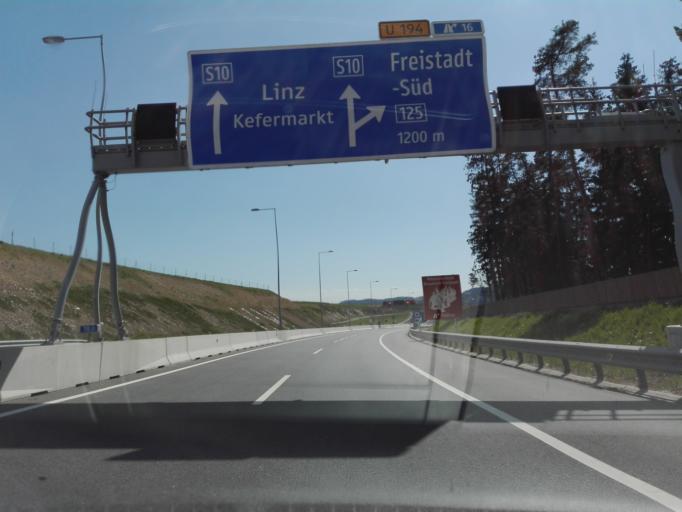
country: AT
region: Upper Austria
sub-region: Politischer Bezirk Freistadt
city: Freistadt
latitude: 48.4962
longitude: 14.5159
